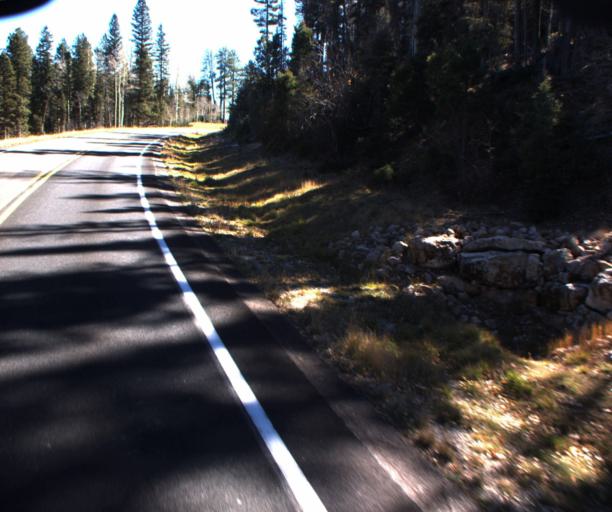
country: US
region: Arizona
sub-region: Coconino County
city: Grand Canyon
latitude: 36.4492
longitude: -112.1312
